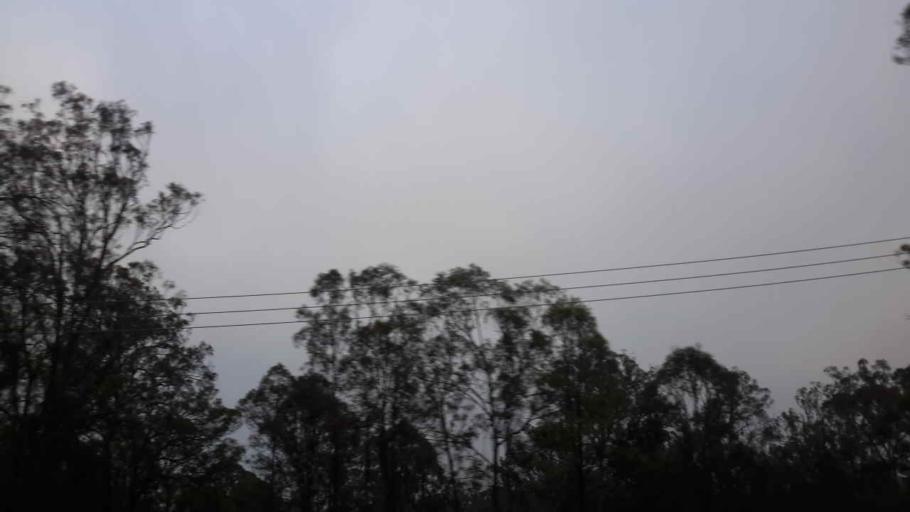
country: AU
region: New South Wales
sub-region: Camden
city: Camden South
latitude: -34.1117
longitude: 150.6961
